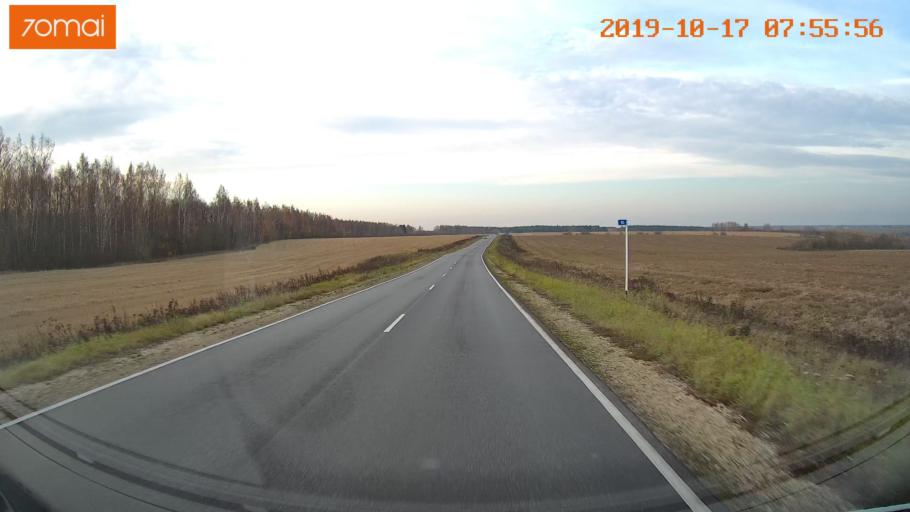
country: RU
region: Vladimir
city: Bavleny
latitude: 56.4294
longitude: 39.5965
